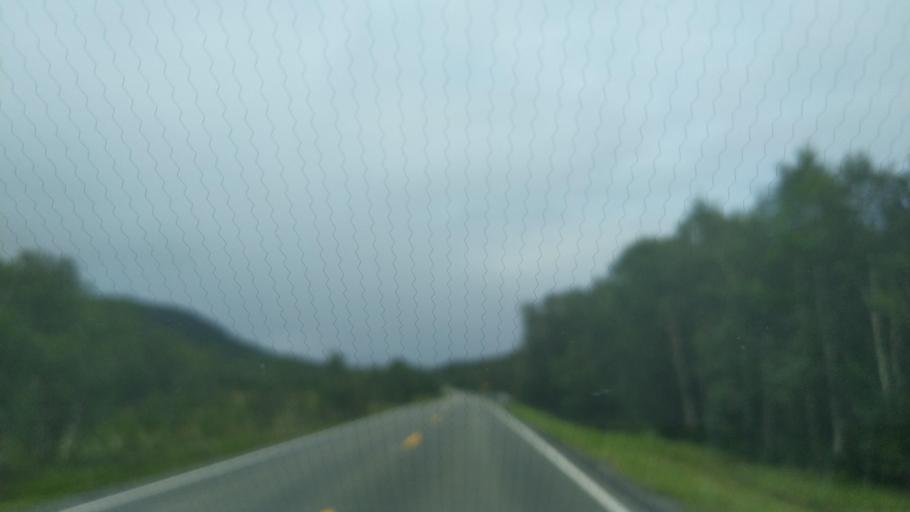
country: NO
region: Nordland
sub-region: Ballangen
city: Ballangen
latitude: 68.4991
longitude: 16.8372
